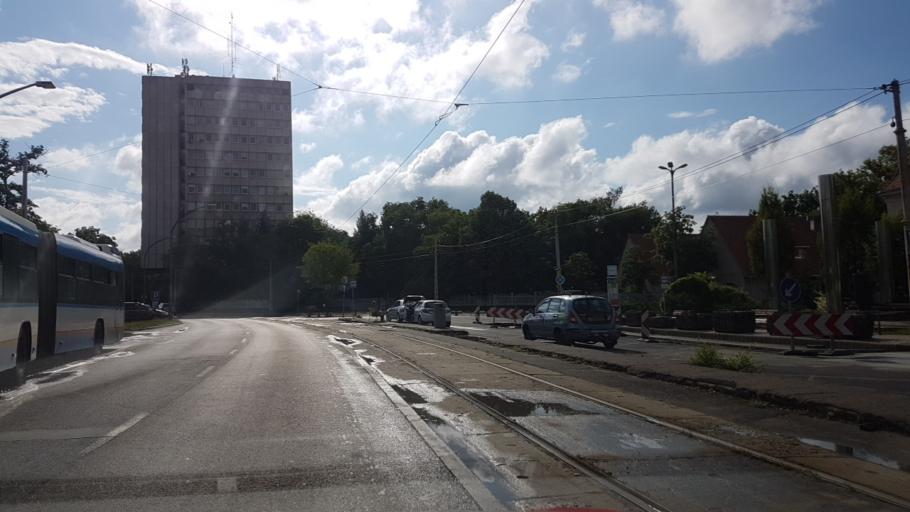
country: HU
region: Hajdu-Bihar
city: Debrecen
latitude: 47.5561
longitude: 21.6290
